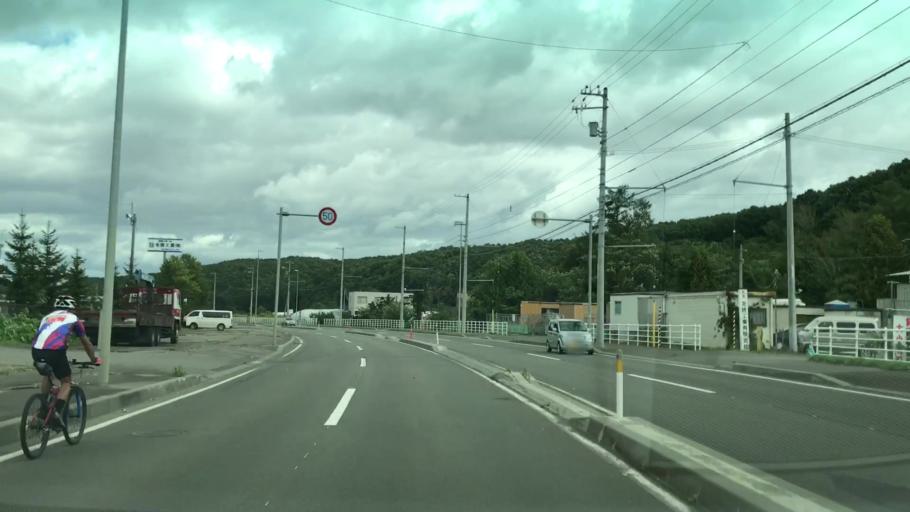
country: JP
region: Hokkaido
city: Kitahiroshima
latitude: 42.9596
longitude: 141.4559
